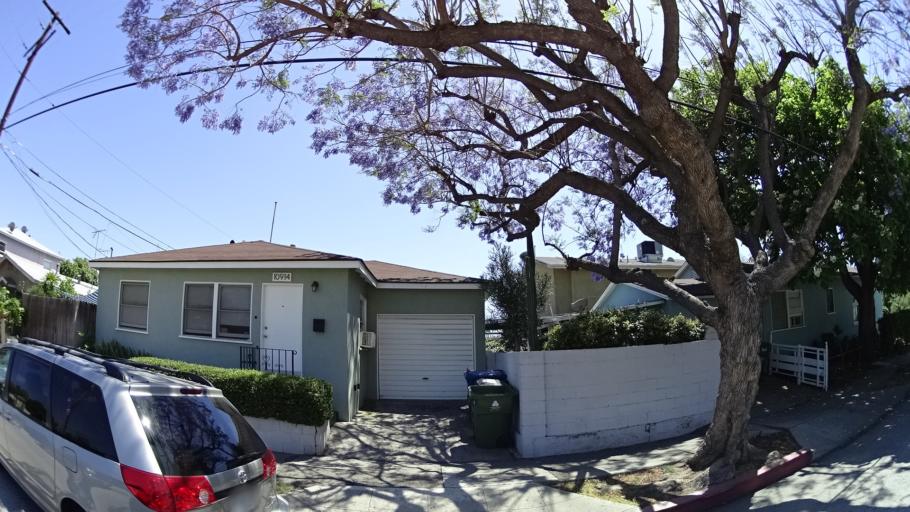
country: US
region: California
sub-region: Los Angeles County
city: North Hollywood
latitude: 34.1739
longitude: -118.3689
